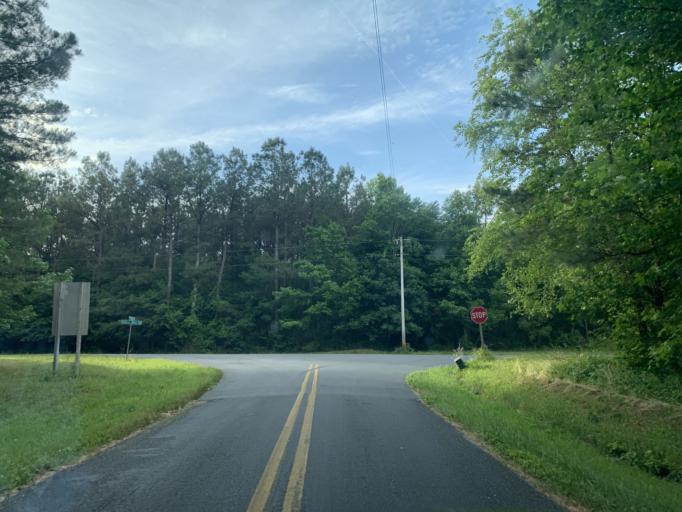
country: US
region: Maryland
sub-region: Worcester County
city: Pocomoke City
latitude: 38.0931
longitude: -75.4646
